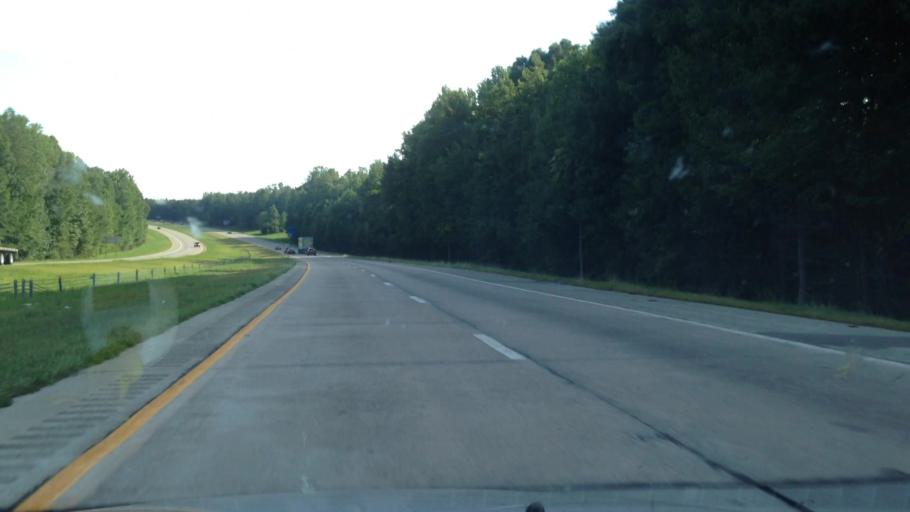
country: US
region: North Carolina
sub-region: Davidson County
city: Midway
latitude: 35.9534
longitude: -80.2344
